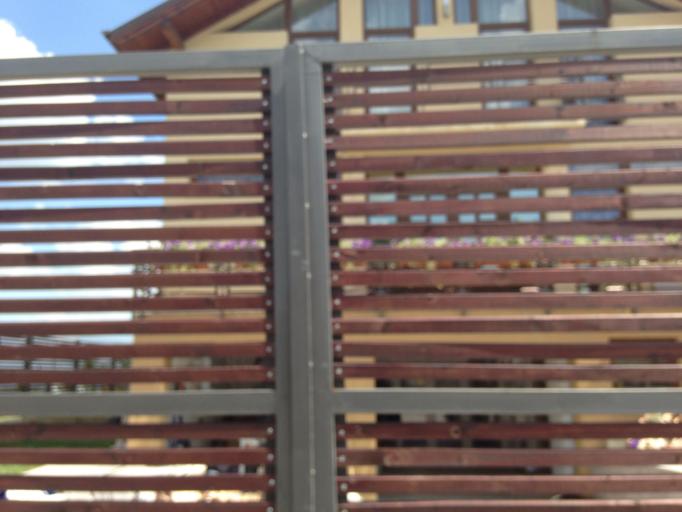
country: RO
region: Cluj
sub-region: Comuna Feleacu
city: Feleacu
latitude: 46.7327
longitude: 23.5901
